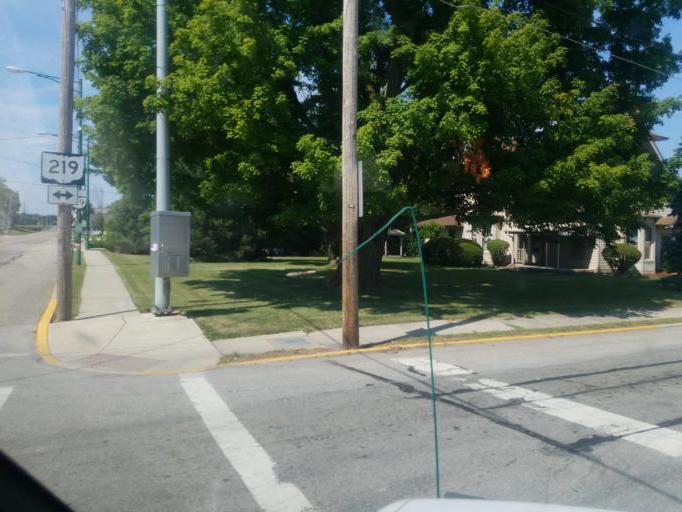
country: US
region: Ohio
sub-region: Auglaize County
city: New Bremen
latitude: 40.4955
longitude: -84.3165
